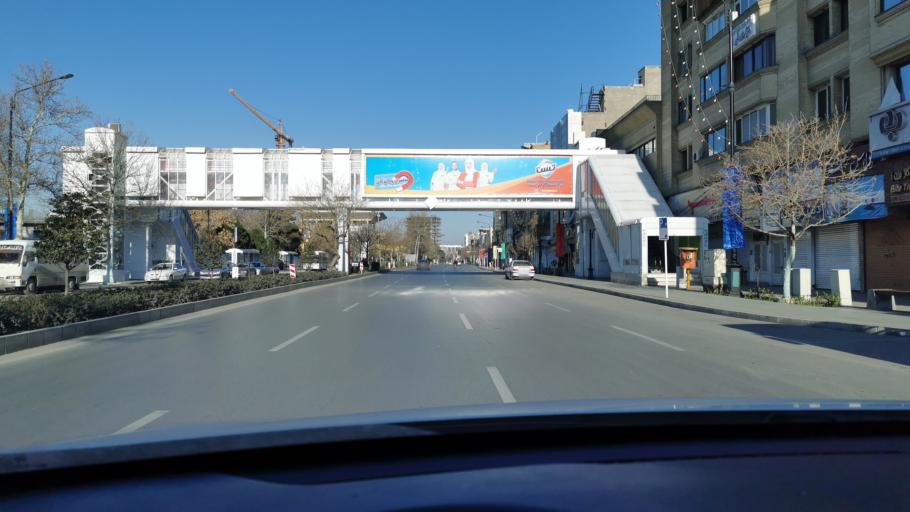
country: IR
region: Razavi Khorasan
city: Mashhad
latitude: 36.2925
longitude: 59.5839
